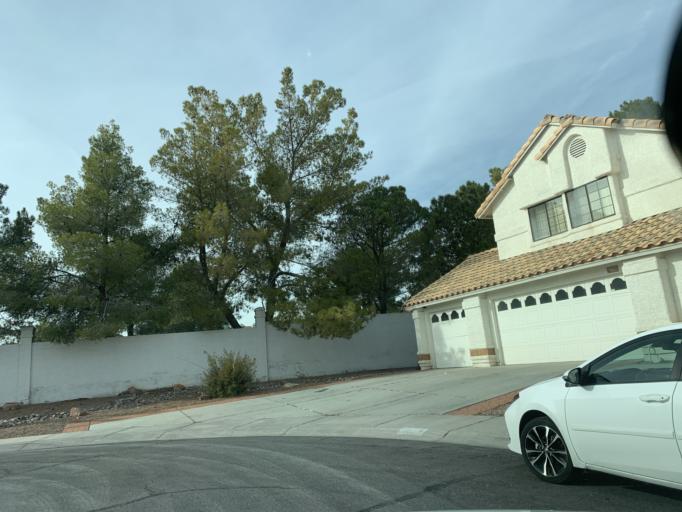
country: US
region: Nevada
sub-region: Clark County
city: Summerlin South
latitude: 36.1349
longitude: -115.3059
